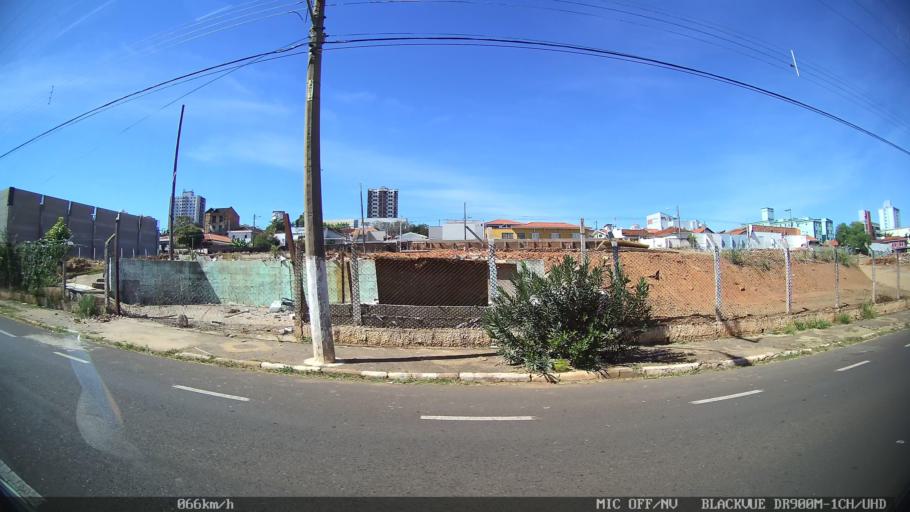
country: BR
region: Sao Paulo
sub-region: Franca
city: Franca
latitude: -20.5326
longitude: -47.4048
